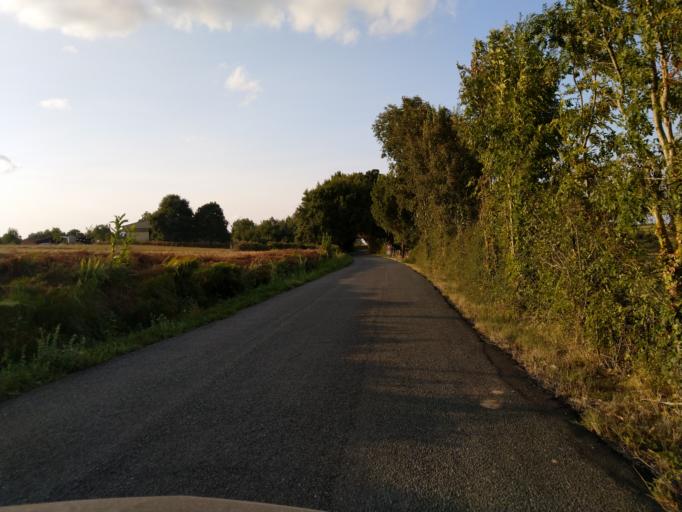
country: FR
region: Midi-Pyrenees
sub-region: Departement du Tarn
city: Frejairolles
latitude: 43.8641
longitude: 2.2334
